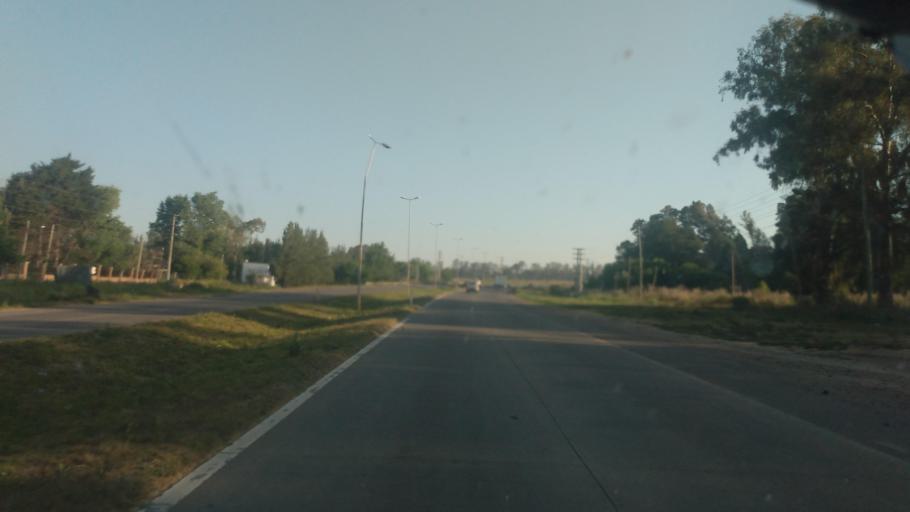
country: AR
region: Buenos Aires
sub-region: Partido de Campana
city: Campana
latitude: -34.2508
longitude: -58.9649
